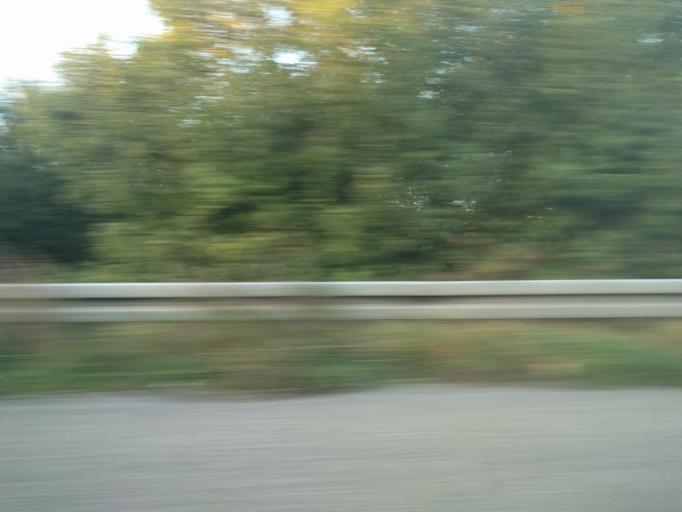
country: DK
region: South Denmark
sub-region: Nyborg Kommune
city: Ullerslev
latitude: 55.3449
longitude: 10.6444
